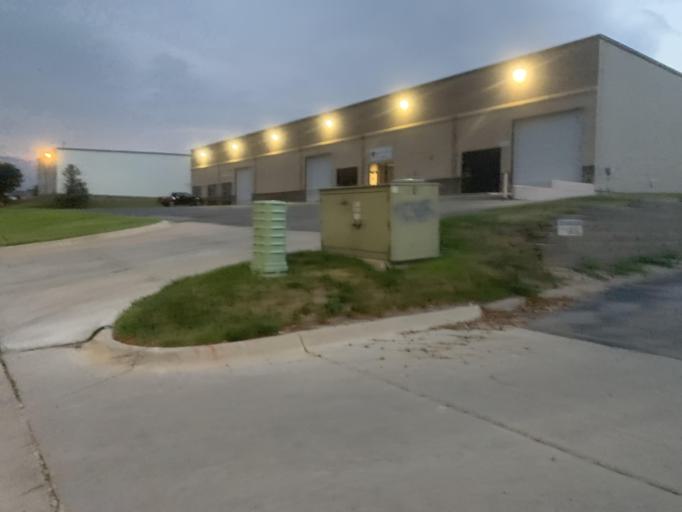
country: US
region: Nebraska
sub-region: Douglas County
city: Ralston
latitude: 41.1882
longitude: -96.0836
